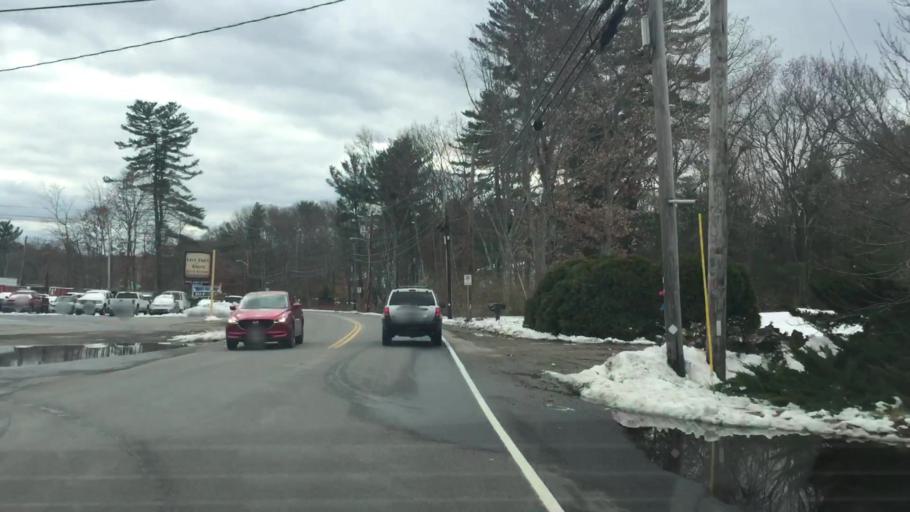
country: US
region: New Hampshire
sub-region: Rockingham County
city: Salem
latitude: 42.7642
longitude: -71.2495
